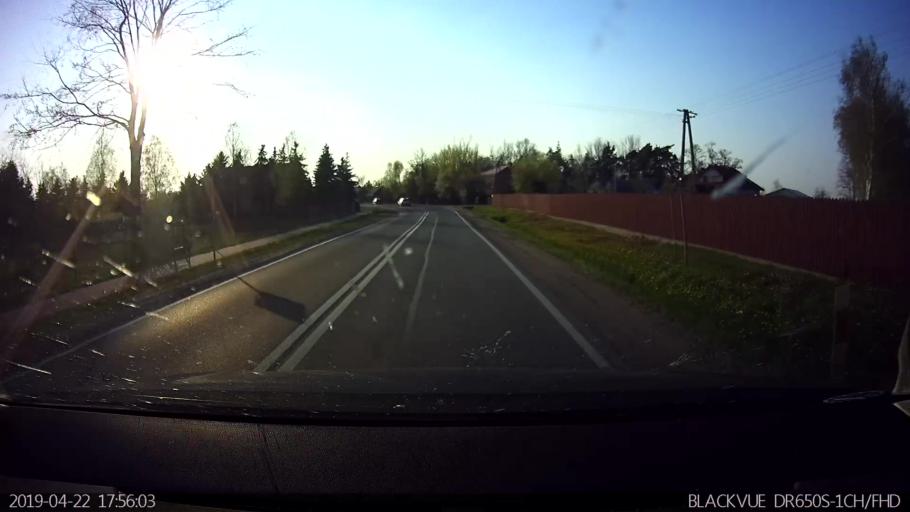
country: PL
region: Masovian Voivodeship
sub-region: Powiat wegrowski
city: Korytnica
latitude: 52.4640
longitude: 21.9123
